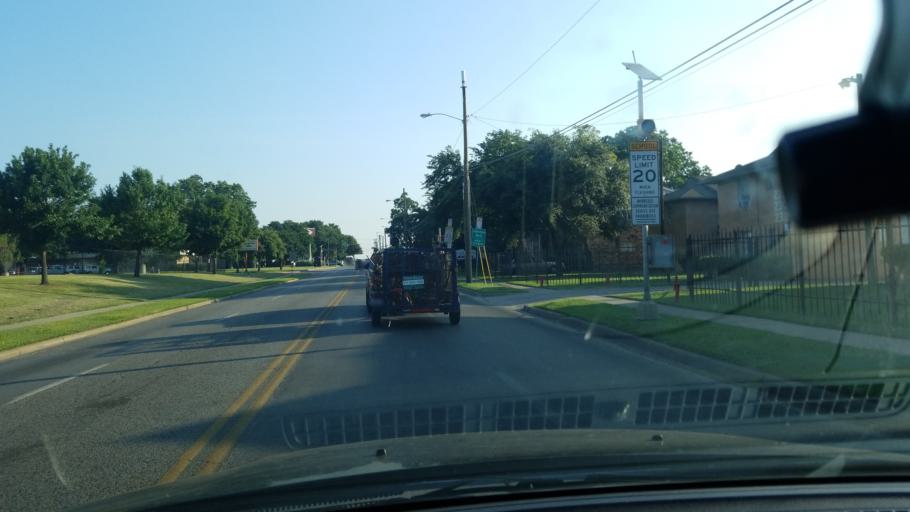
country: US
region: Texas
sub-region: Dallas County
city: Dallas
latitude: 32.7451
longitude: -96.8156
